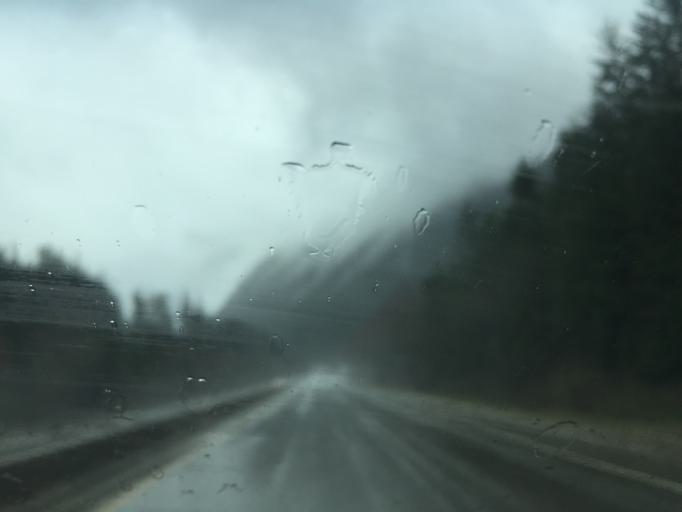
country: CA
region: British Columbia
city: Hope
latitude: 49.5290
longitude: -121.2055
